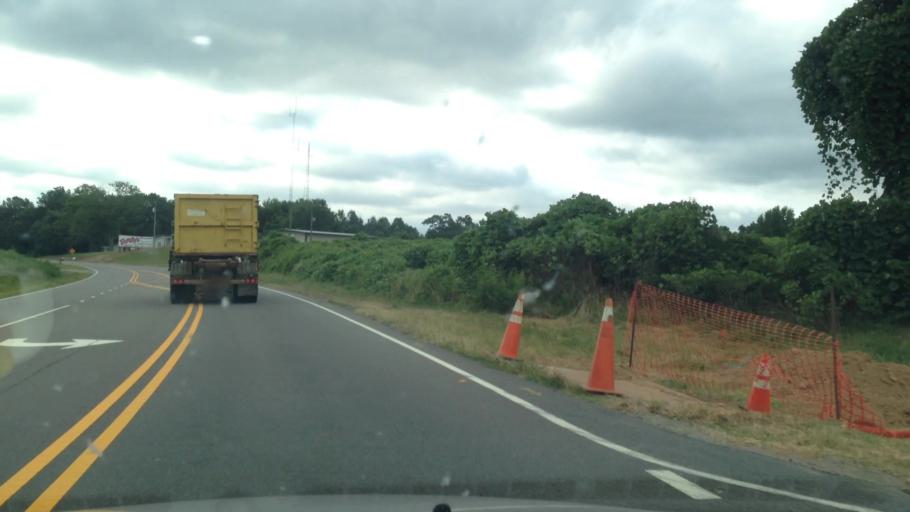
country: US
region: North Carolina
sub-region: Rockingham County
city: Wentworth
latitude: 36.3722
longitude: -79.7315
